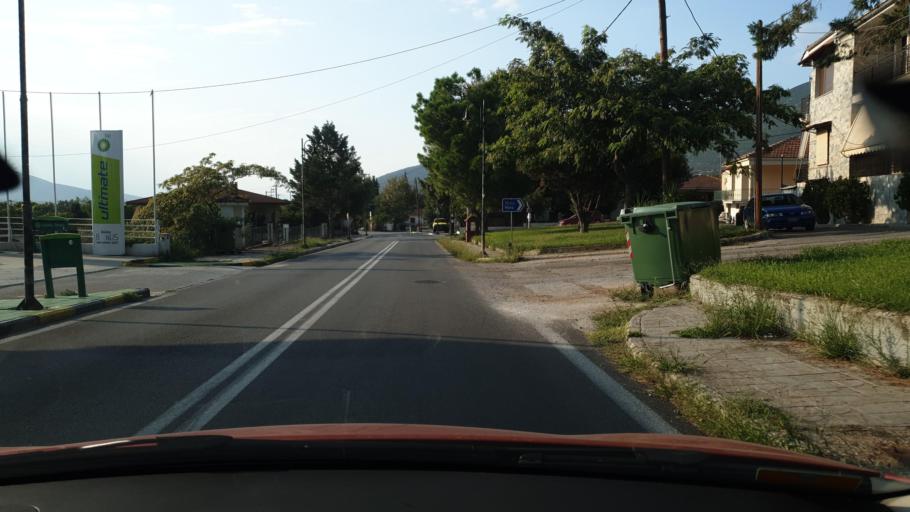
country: GR
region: Thessaly
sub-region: Nomos Magnisias
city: Sourpi
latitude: 39.0974
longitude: 22.8994
